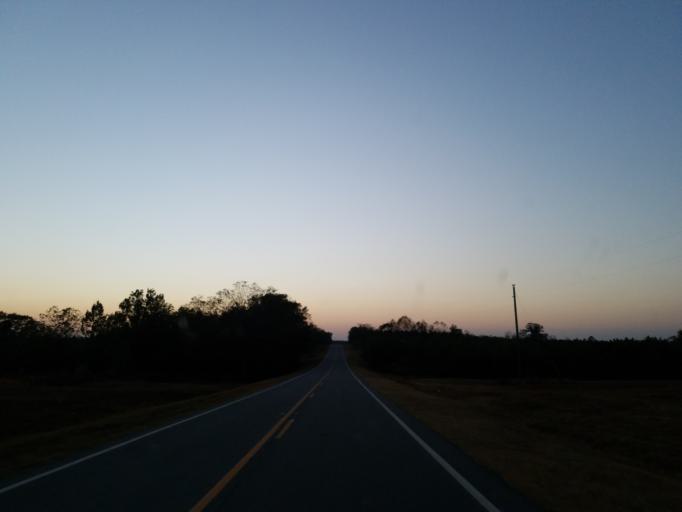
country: US
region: Georgia
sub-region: Wilcox County
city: Rochelle
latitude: 31.8159
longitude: -83.5209
